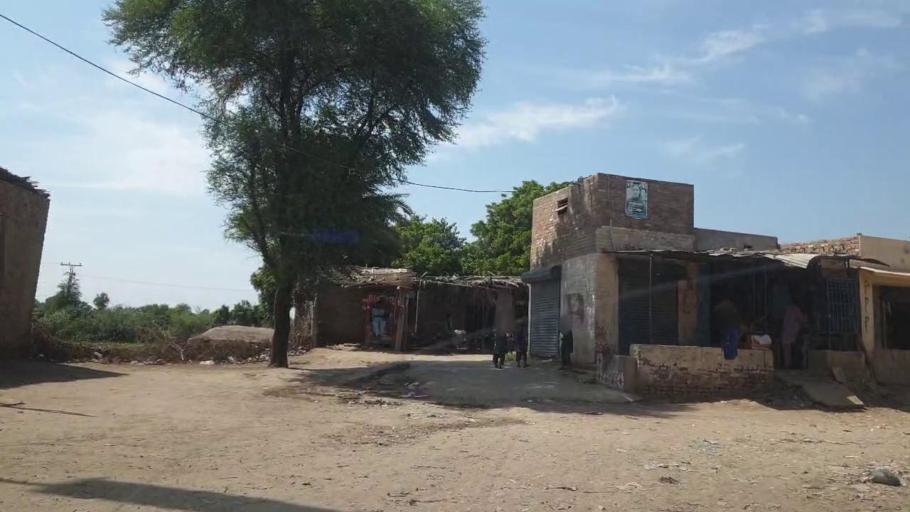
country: PK
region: Sindh
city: Tando Jam
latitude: 25.3990
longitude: 68.5878
